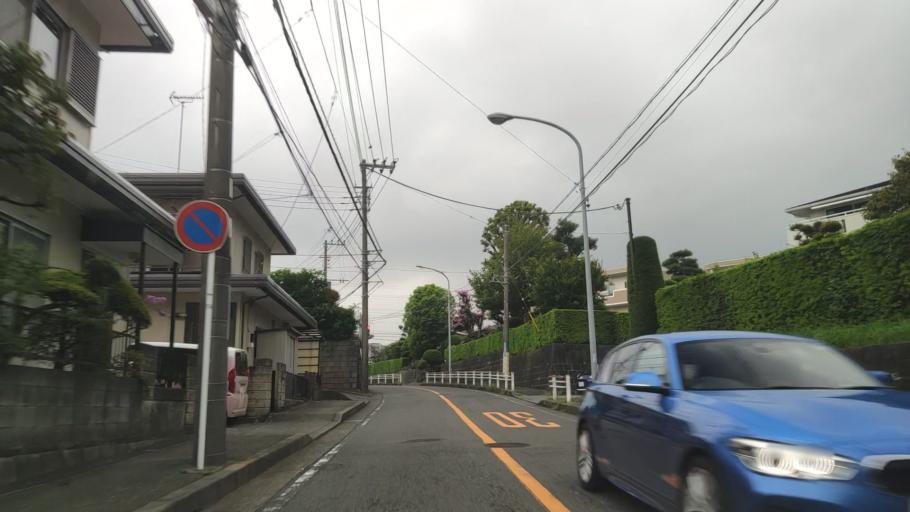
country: JP
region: Kanagawa
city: Minami-rinkan
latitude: 35.4482
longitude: 139.5023
